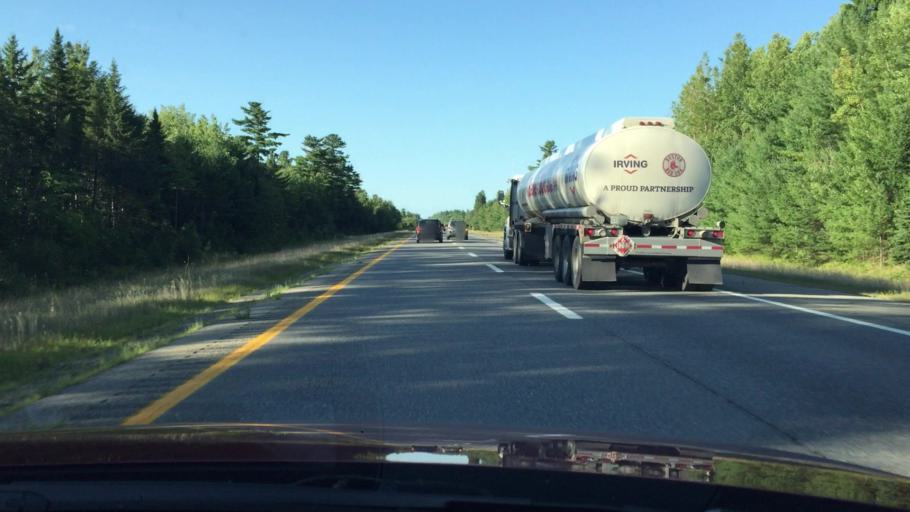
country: US
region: Maine
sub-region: Penobscot County
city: Lincoln
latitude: 45.3879
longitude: -68.6034
